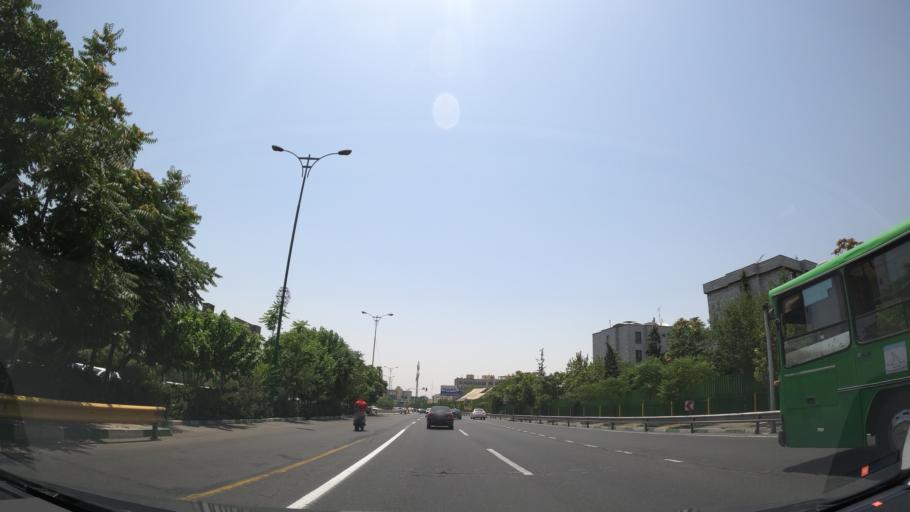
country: IR
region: Tehran
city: Tehran
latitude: 35.7213
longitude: 51.3790
